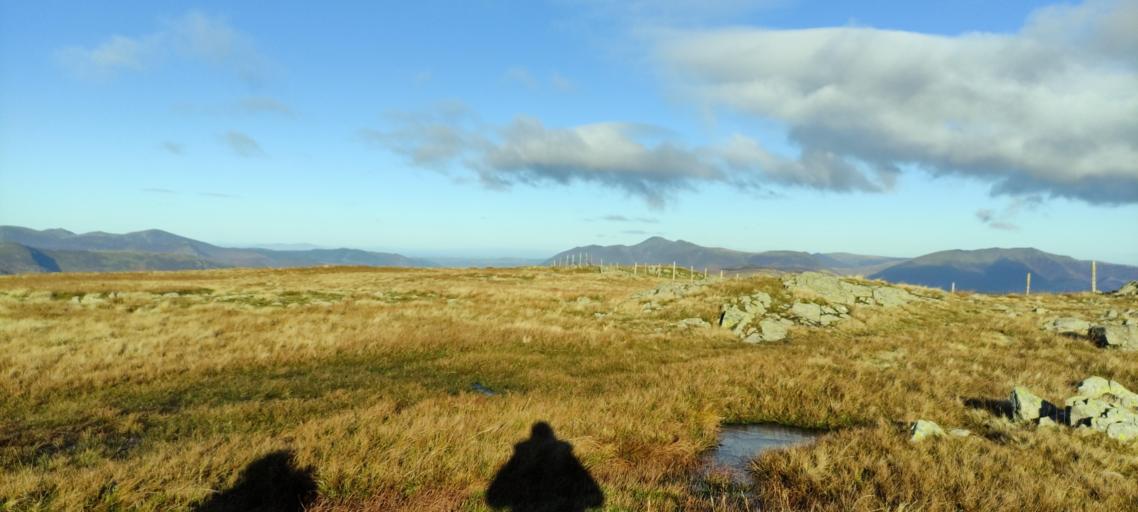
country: GB
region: England
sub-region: Cumbria
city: Keswick
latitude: 54.5033
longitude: -3.0962
